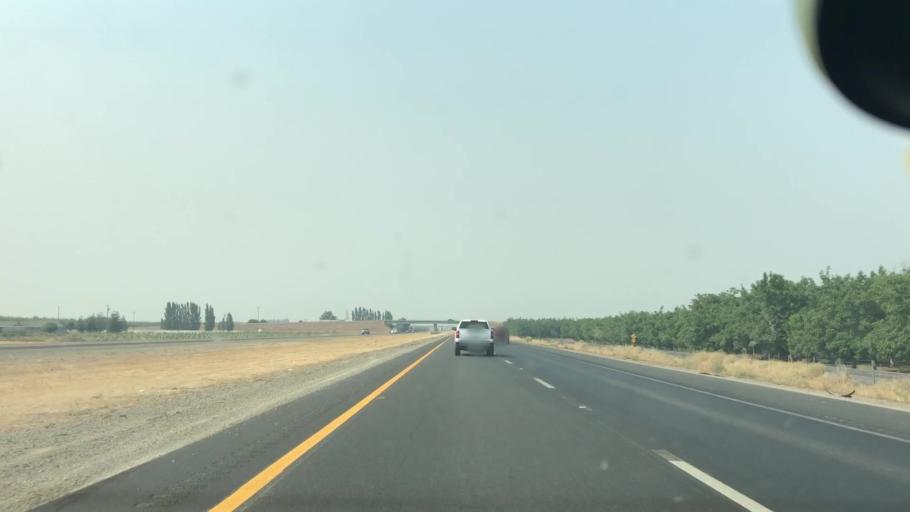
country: US
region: California
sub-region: San Joaquin County
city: Tracy
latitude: 37.6633
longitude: -121.3429
